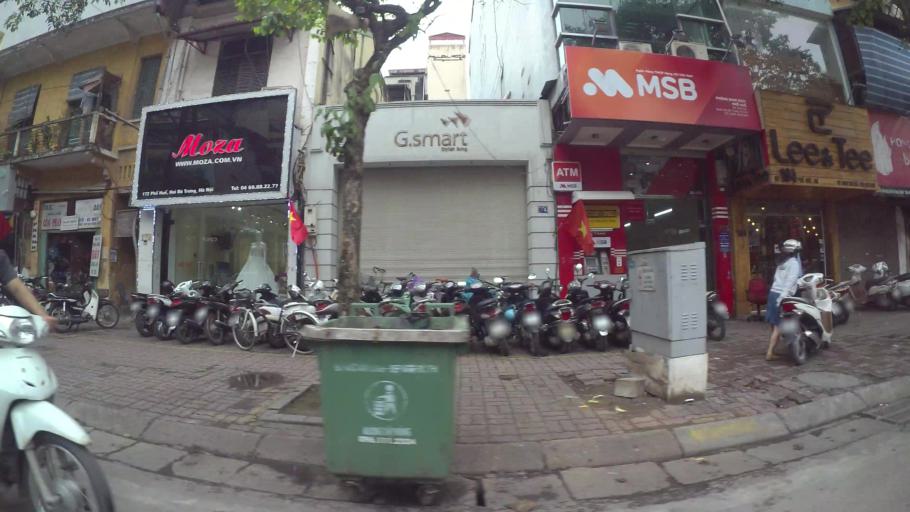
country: VN
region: Ha Noi
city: Hai BaTrung
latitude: 21.0146
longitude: 105.8516
